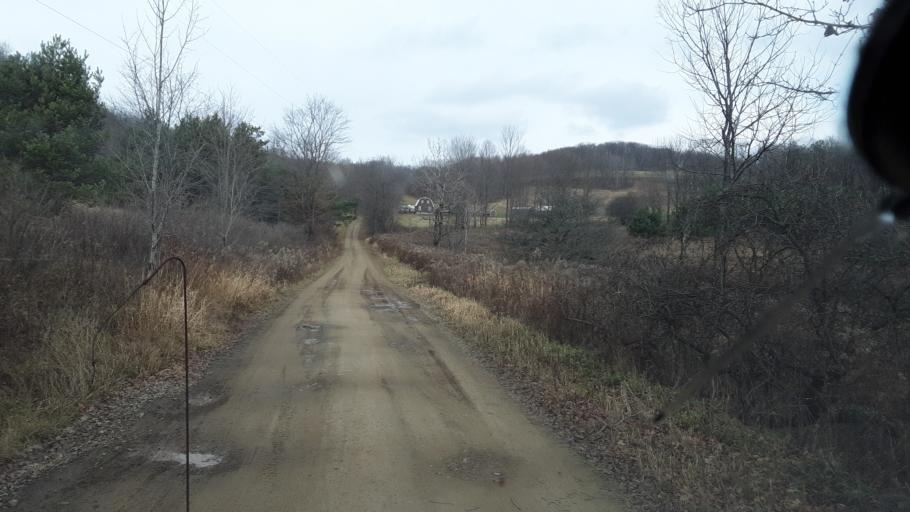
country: US
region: Pennsylvania
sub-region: Tioga County
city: Westfield
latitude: 41.9140
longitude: -77.7063
